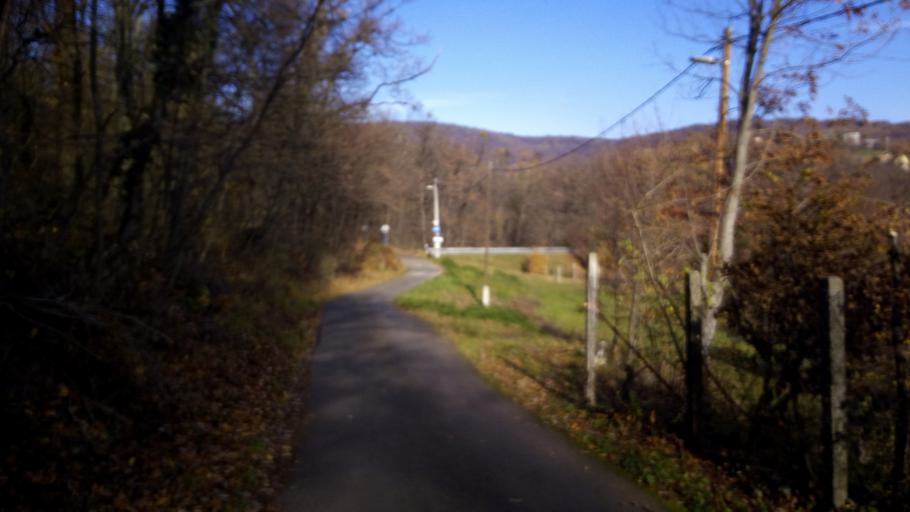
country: HU
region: Baranya
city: Pecs
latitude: 46.0957
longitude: 18.1809
